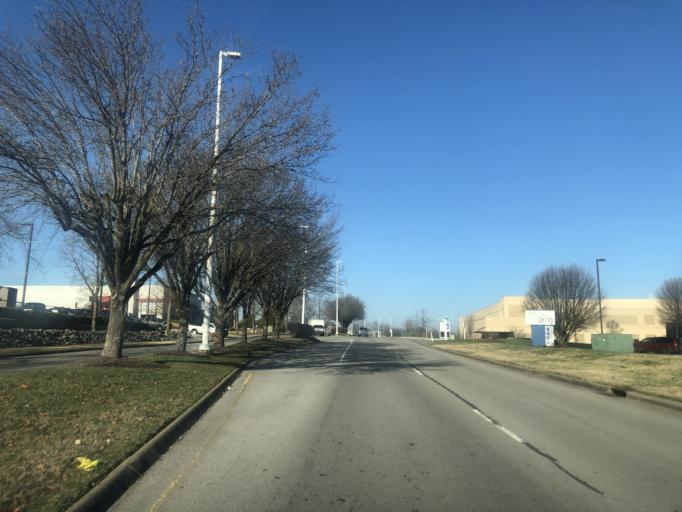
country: US
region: Tennessee
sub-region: Rutherford County
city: La Vergne
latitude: 36.0371
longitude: -86.6424
